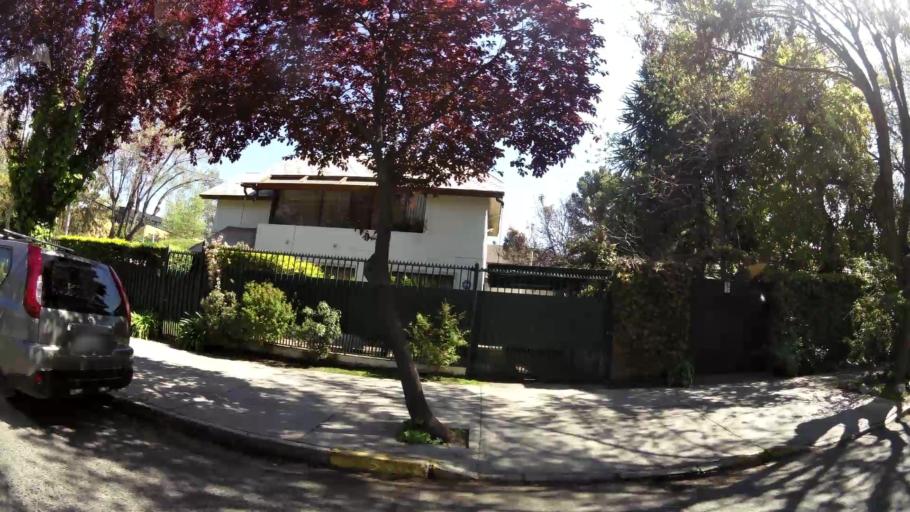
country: CL
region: Santiago Metropolitan
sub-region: Provincia de Santiago
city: Villa Presidente Frei, Nunoa, Santiago, Chile
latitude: -33.4237
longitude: -70.5554
